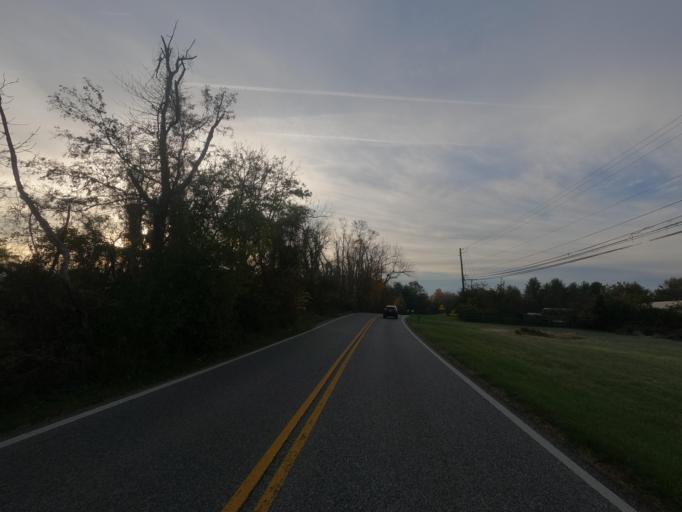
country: US
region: Maryland
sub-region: Montgomery County
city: Ashton-Sandy Spring
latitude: 39.1356
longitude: -77.0314
